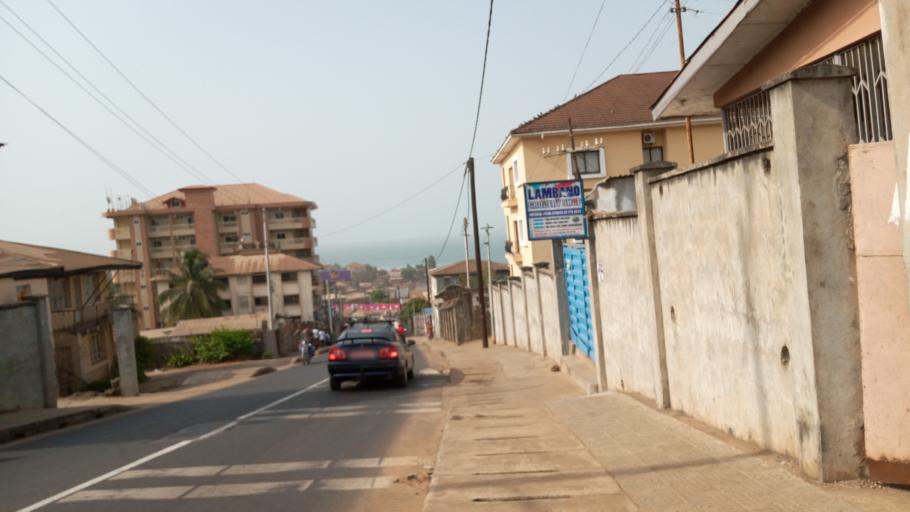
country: SL
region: Western Area
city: Freetown
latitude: 8.4815
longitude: -13.2587
